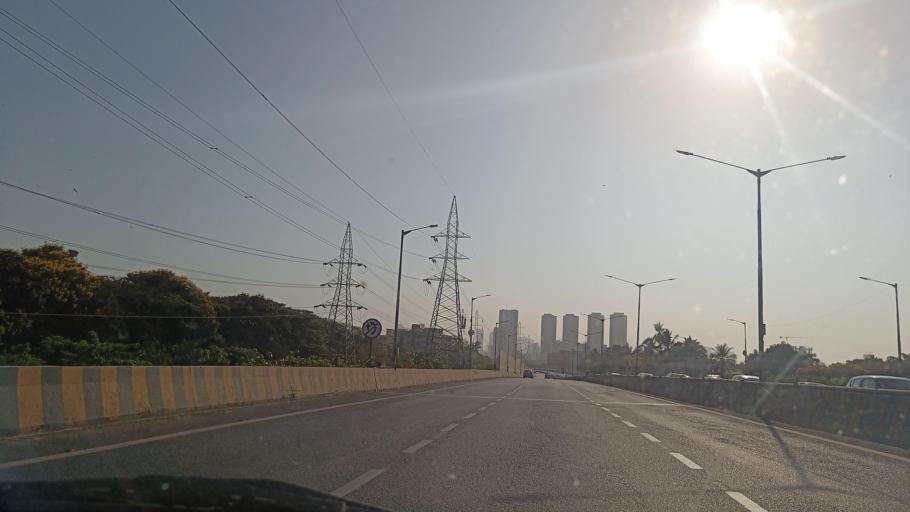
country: IN
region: Maharashtra
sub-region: Mumbai Suburban
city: Mumbai
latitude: 19.0321
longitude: 72.8945
